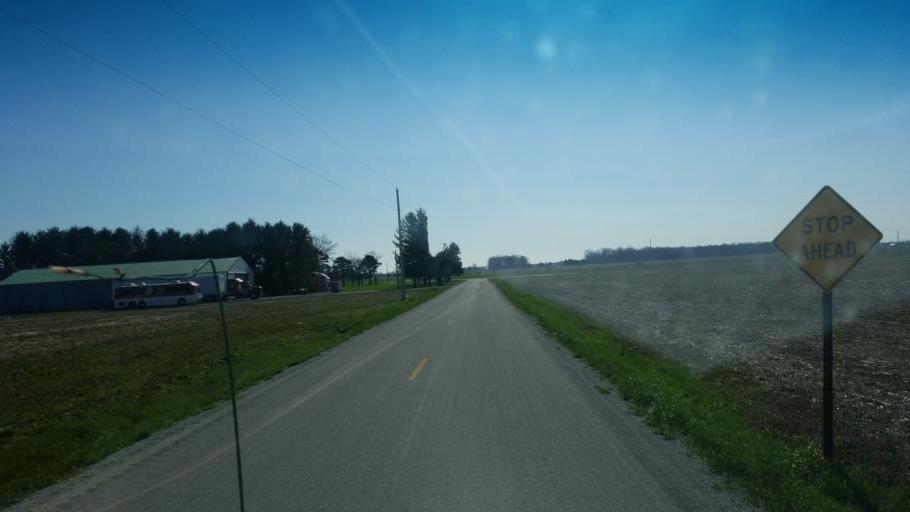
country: US
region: Ohio
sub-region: Hardin County
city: Kenton
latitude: 40.7017
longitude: -83.5406
